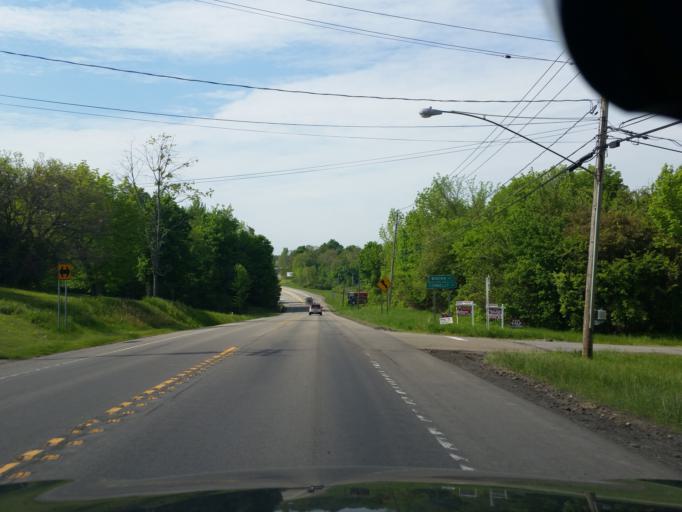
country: US
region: New York
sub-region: Chautauqua County
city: Lakewood
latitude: 42.1426
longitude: -79.4017
